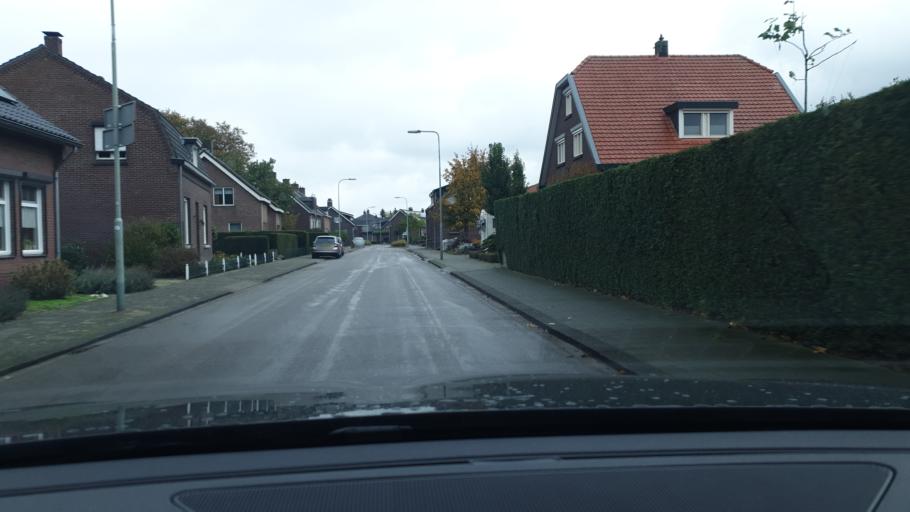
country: NL
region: Limburg
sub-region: Gemeente Peel en Maas
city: Maasbree
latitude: 51.4116
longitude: 6.0299
